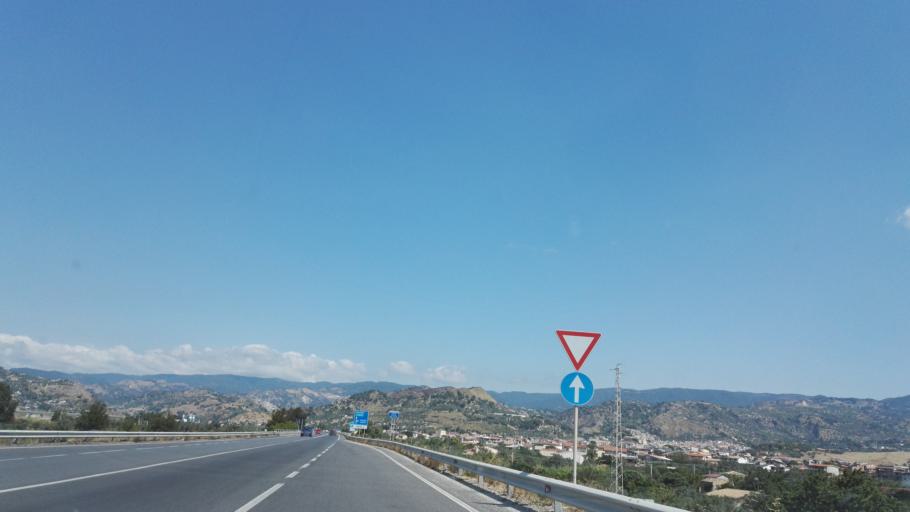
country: IT
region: Calabria
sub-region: Provincia di Reggio Calabria
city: Gioiosa Ionica
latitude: 38.3127
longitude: 16.3031
